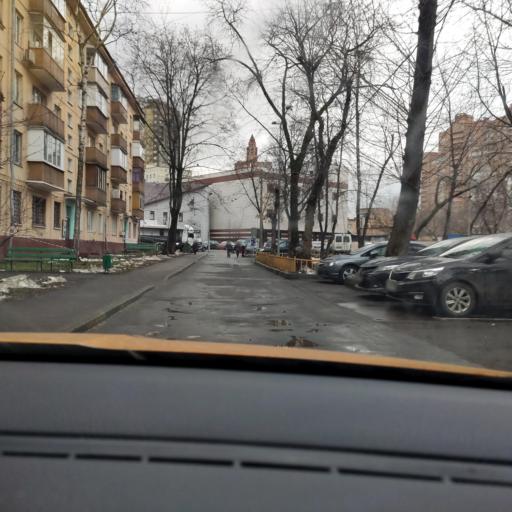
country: RU
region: Moscow
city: Novokuz'minki
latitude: 55.7120
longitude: 37.7711
